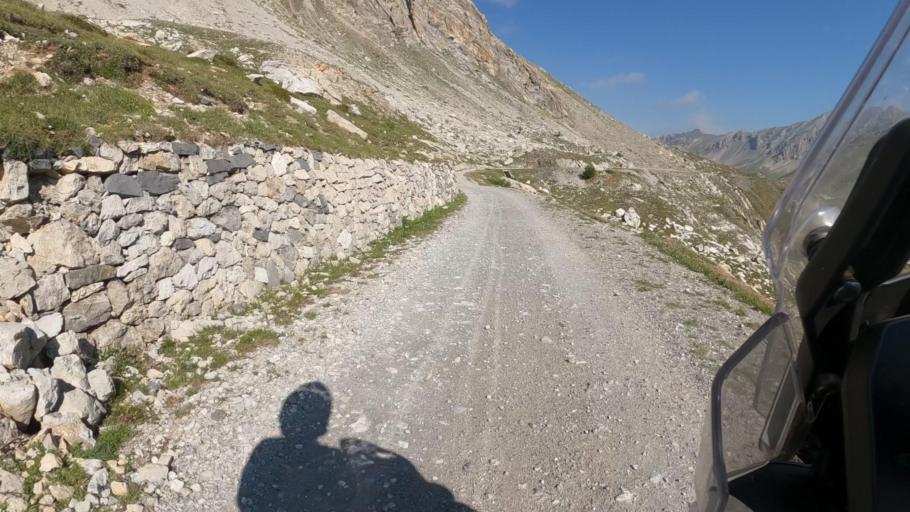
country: IT
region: Piedmont
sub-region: Provincia di Cuneo
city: Pietraporzio
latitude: 44.3925
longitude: 7.0253
